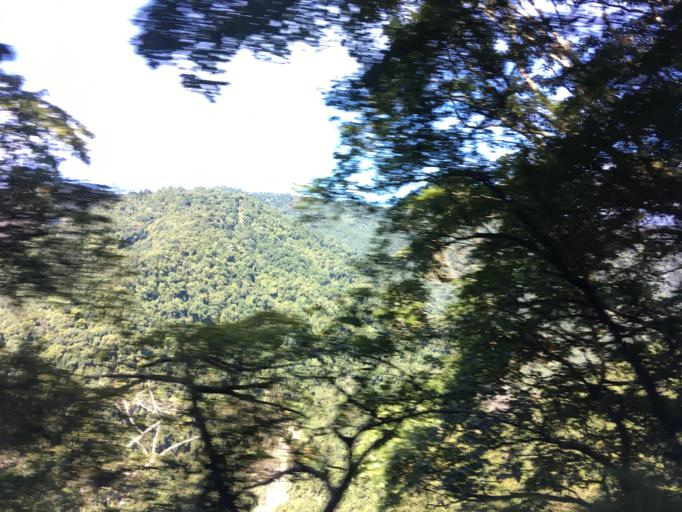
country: TW
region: Taiwan
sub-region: Yilan
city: Yilan
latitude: 24.5534
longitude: 121.5100
